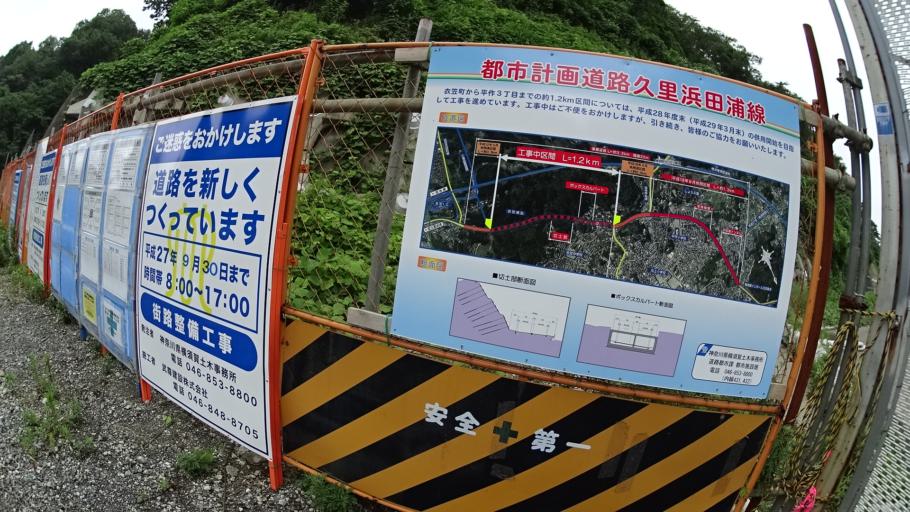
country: JP
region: Kanagawa
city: Yokosuka
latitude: 35.2468
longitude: 139.6573
